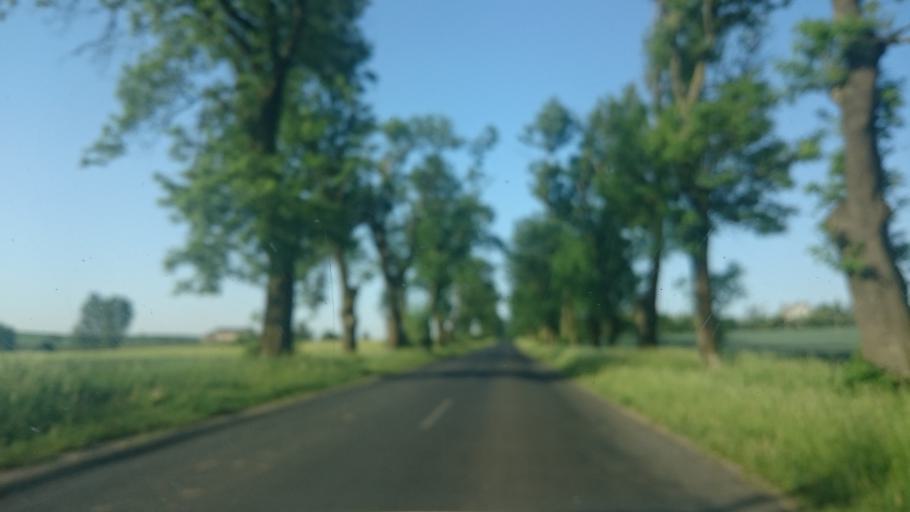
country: PL
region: Kujawsko-Pomorskie
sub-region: Powiat golubsko-dobrzynski
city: Zbojno
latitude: 52.9903
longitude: 19.1236
